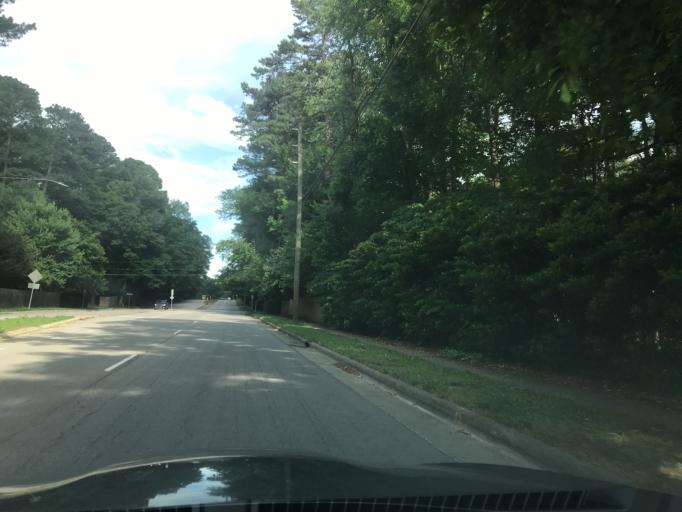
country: US
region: North Carolina
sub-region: Wake County
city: West Raleigh
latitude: 35.8617
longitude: -78.6935
